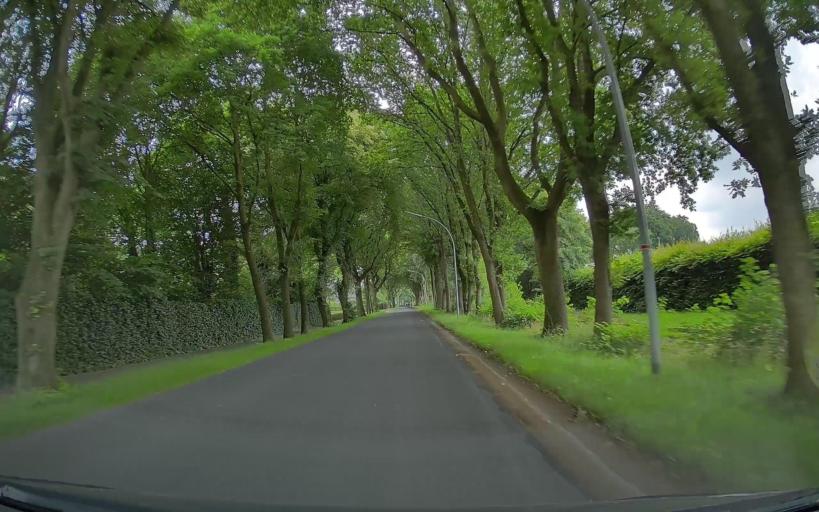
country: DE
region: Lower Saxony
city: Bosel
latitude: 52.9991
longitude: 7.9489
